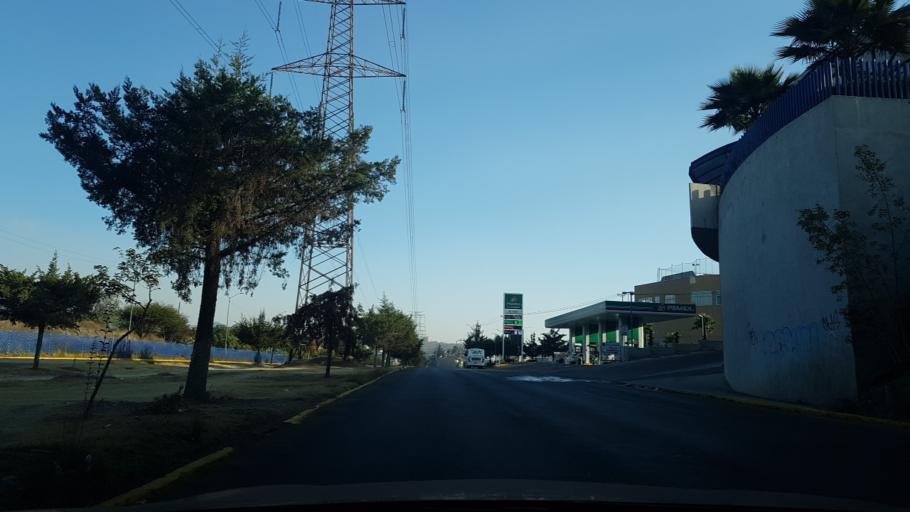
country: MX
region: Mexico
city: Cuautitlan Izcalli
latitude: 19.6410
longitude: -99.2232
